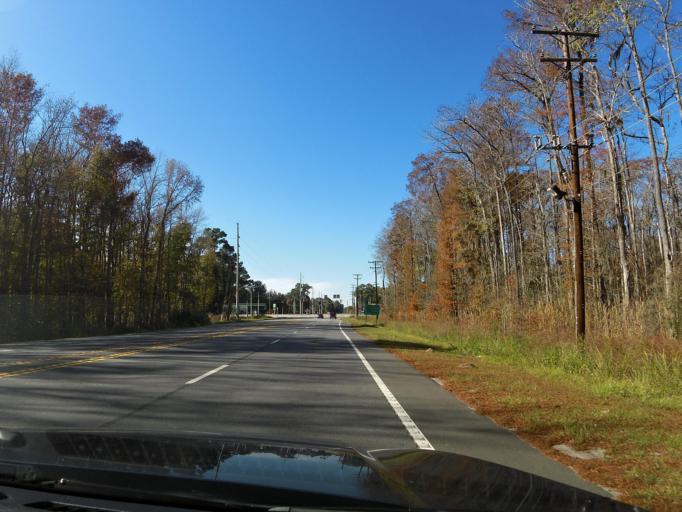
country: US
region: Georgia
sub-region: Liberty County
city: Midway
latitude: 31.7999
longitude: -81.4306
